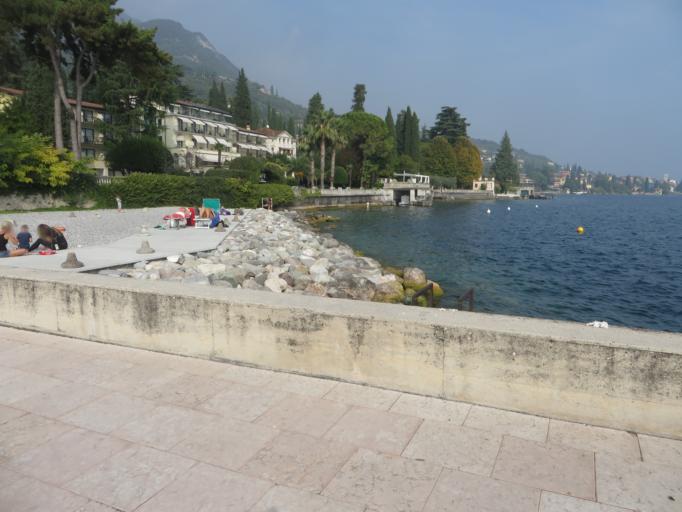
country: IT
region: Lombardy
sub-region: Provincia di Brescia
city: Gardone Riviera
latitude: 45.6220
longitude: 10.5708
